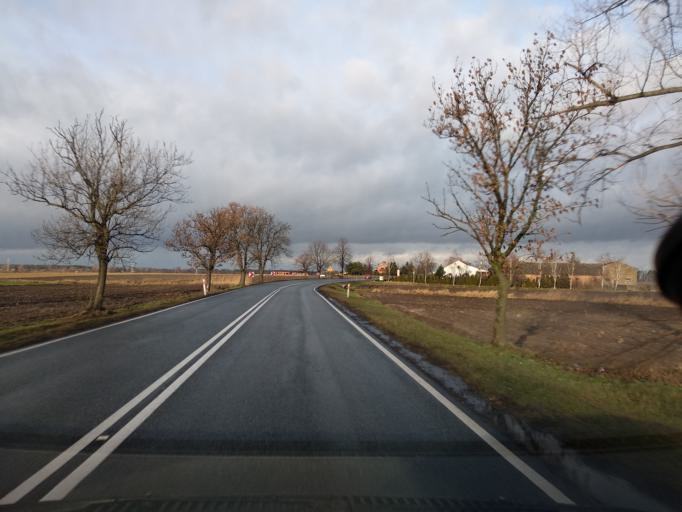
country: PL
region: Greater Poland Voivodeship
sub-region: Powiat koninski
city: Rychwal
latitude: 52.0999
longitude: 18.1672
